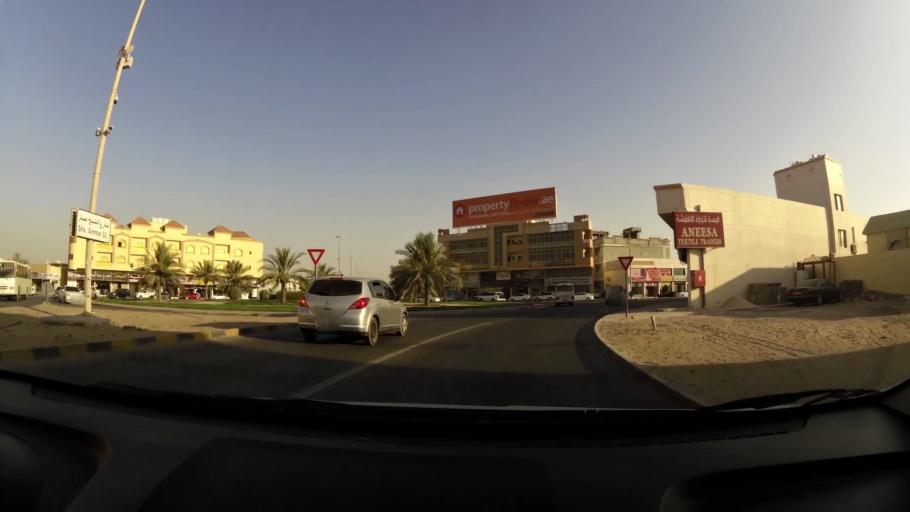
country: AE
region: Ajman
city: Ajman
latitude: 25.3942
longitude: 55.5051
